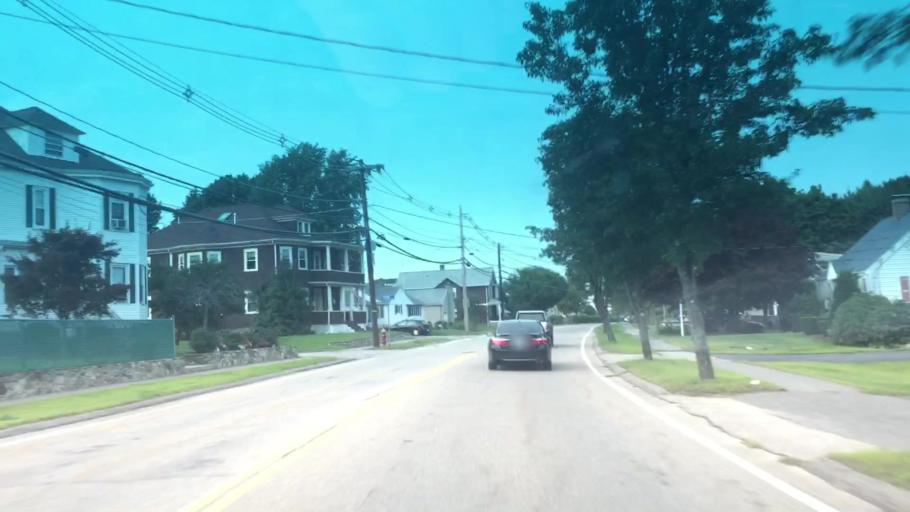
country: US
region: Massachusetts
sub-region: Norfolk County
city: Norwood
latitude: 42.1819
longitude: -71.1974
